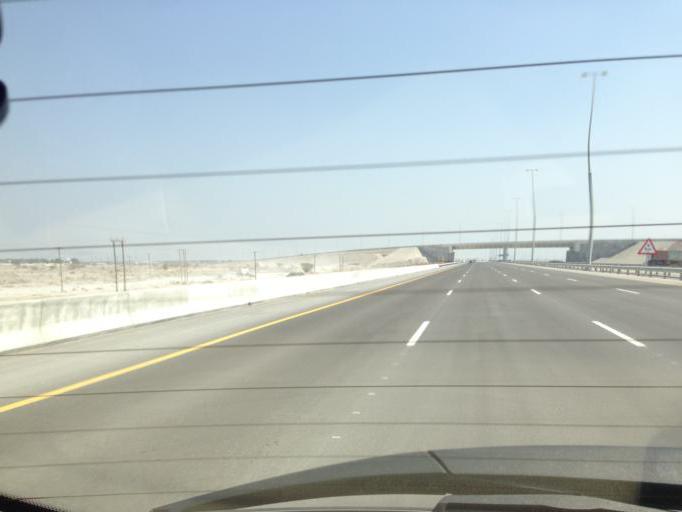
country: OM
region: Al Batinah
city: Barka'
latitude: 23.6217
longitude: 57.8420
